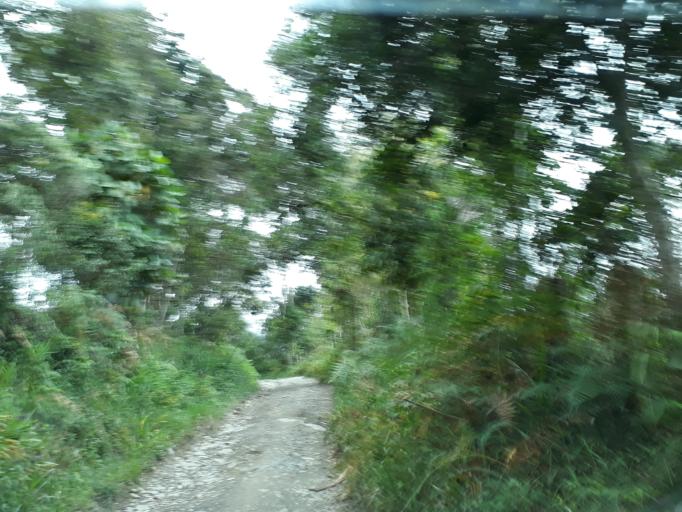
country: CO
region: Boyaca
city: Muzo
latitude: 5.3849
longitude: -74.0973
